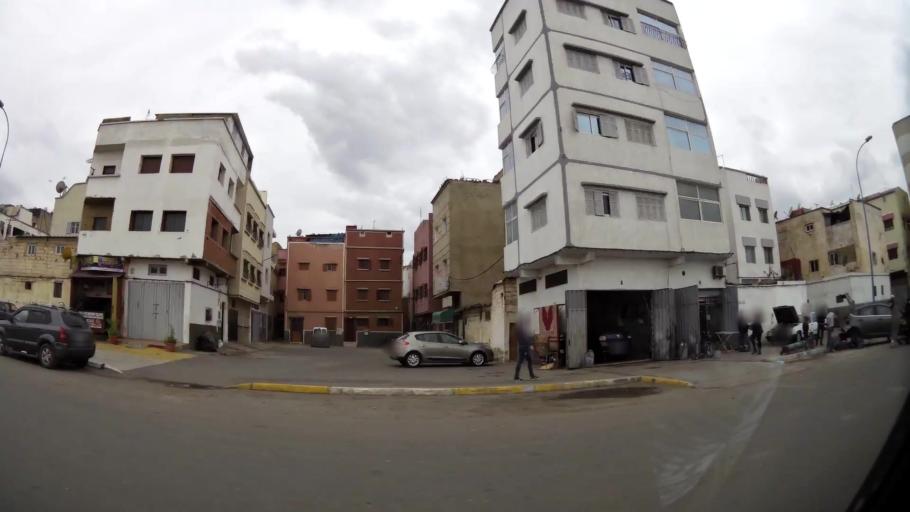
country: MA
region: Grand Casablanca
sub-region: Casablanca
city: Casablanca
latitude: 33.5678
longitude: -7.5658
